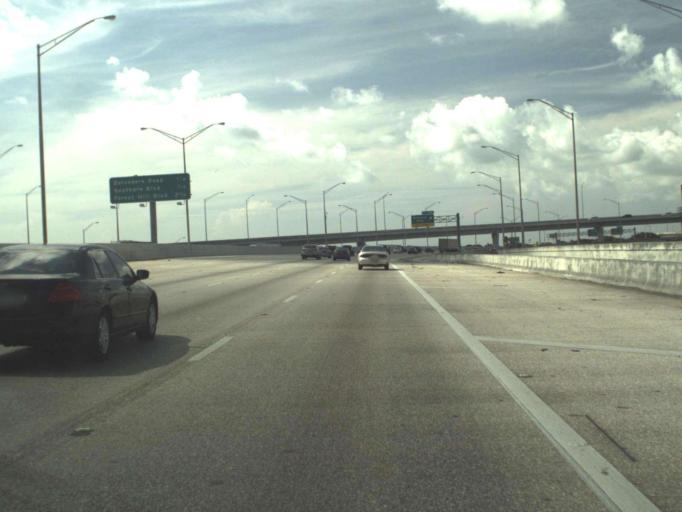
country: US
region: Florida
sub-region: Palm Beach County
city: West Palm Beach
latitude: 26.6938
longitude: -80.0684
